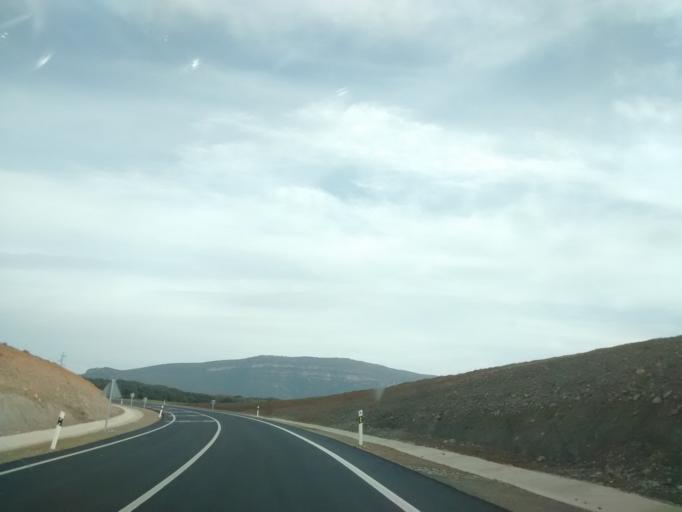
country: ES
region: Aragon
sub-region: Provincia de Zaragoza
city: Siguees
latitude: 42.6118
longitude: -1.0419
